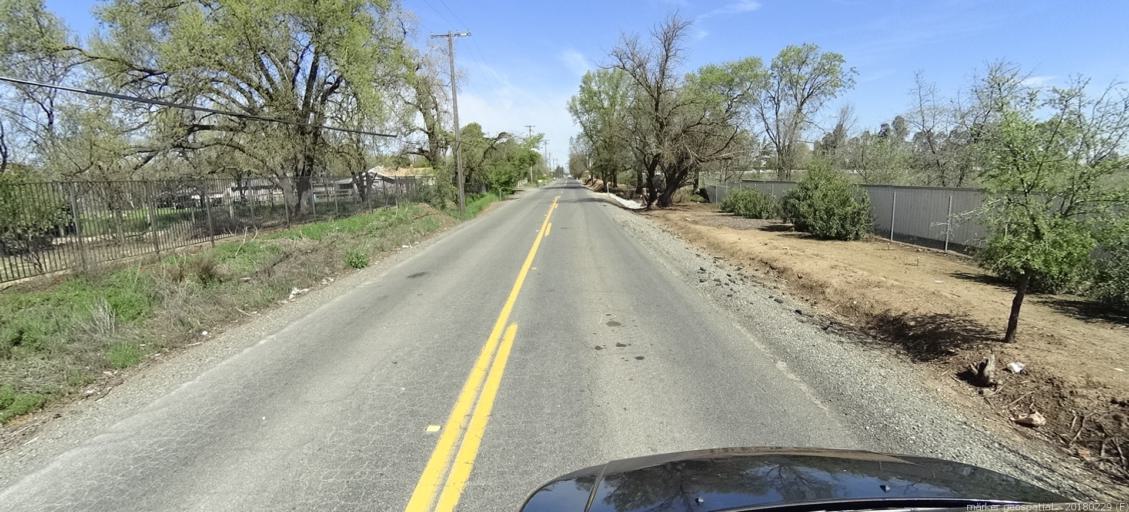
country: US
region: California
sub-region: Sacramento County
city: Rosemont
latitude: 38.5198
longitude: -121.3628
